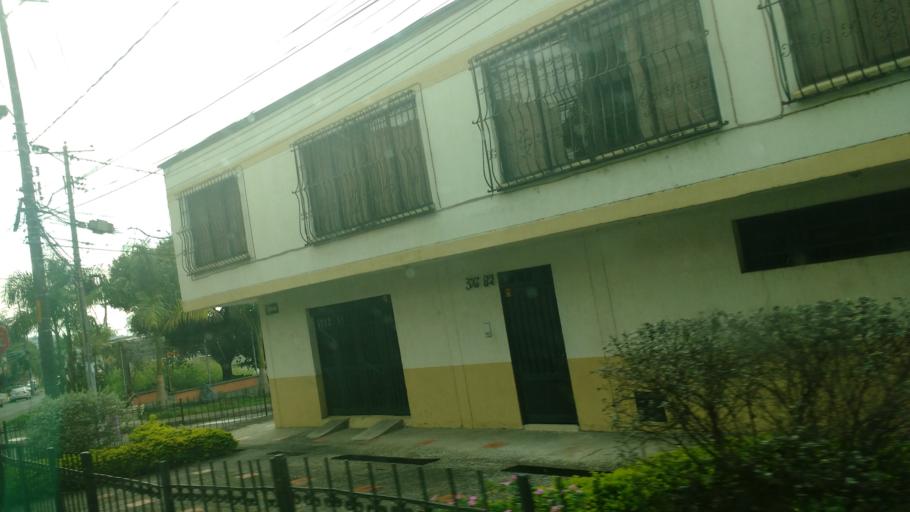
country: CO
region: Risaralda
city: Pereira
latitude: 4.8133
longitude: -75.7094
